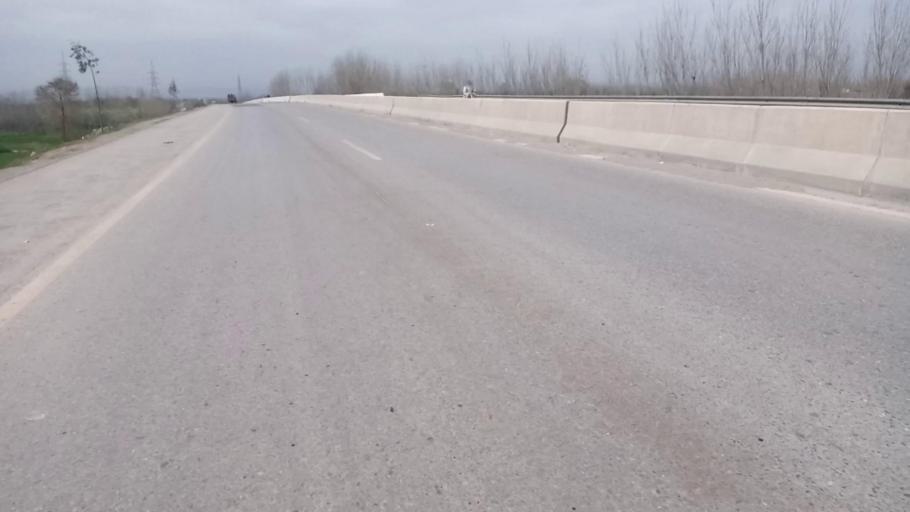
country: PK
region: Khyber Pakhtunkhwa
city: Peshawar
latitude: 34.0594
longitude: 71.6080
